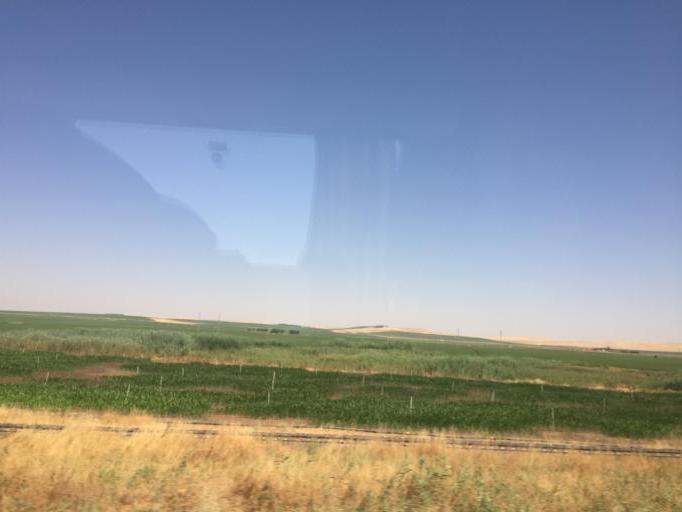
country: TR
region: Diyarbakir
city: Tepe
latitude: 37.8505
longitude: 40.7721
